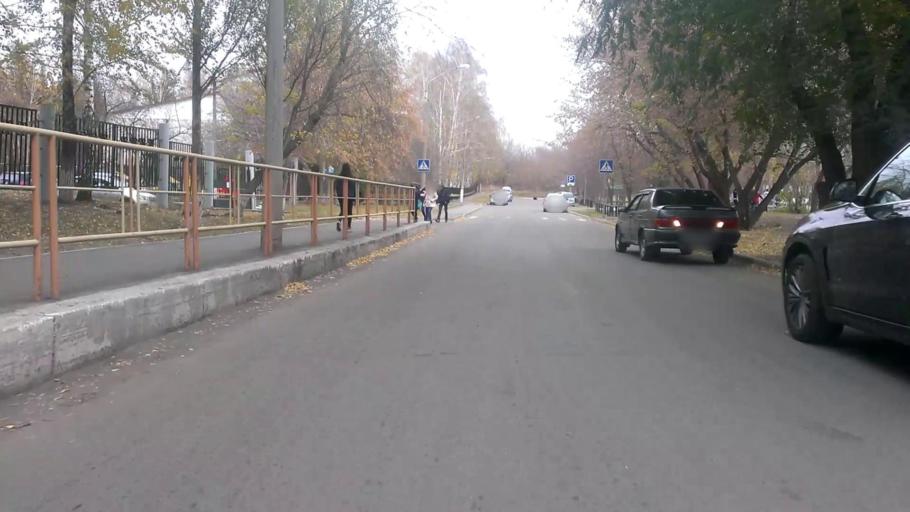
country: RU
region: Altai Krai
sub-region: Gorod Barnaulskiy
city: Barnaul
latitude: 53.3661
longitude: 83.7182
